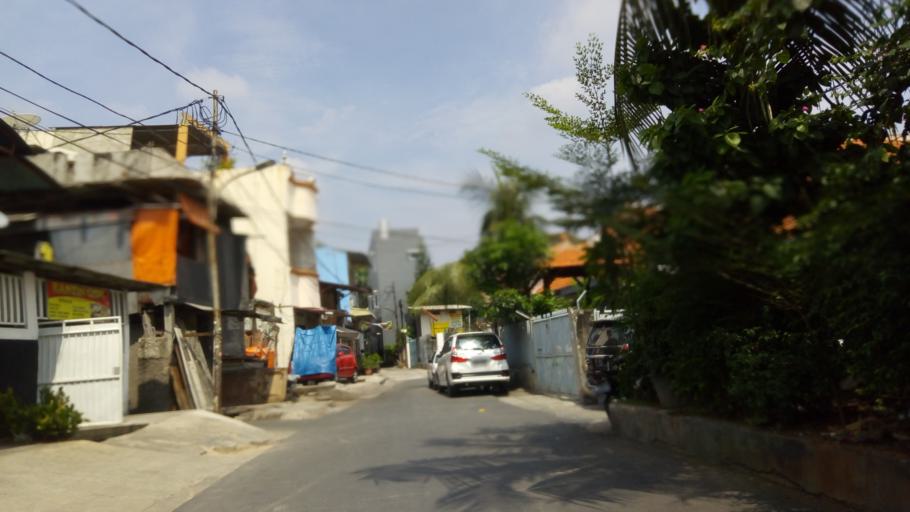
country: ID
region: Jakarta Raya
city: Jakarta
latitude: -6.1496
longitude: 106.8301
